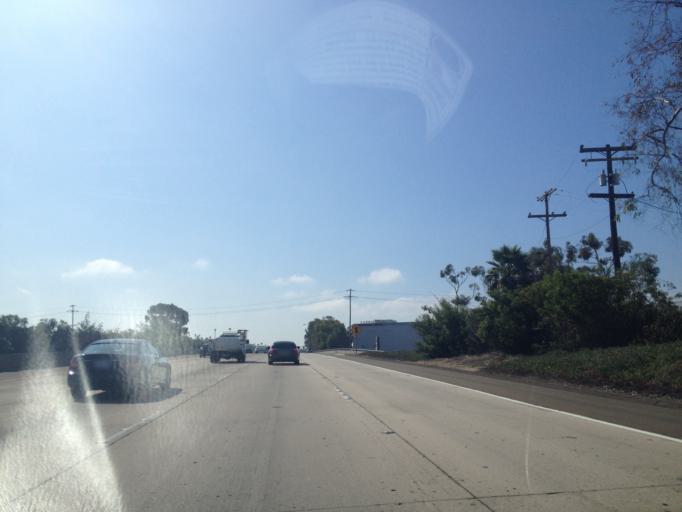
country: US
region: California
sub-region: San Diego County
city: La Jolla
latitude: 32.8083
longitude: -117.2173
